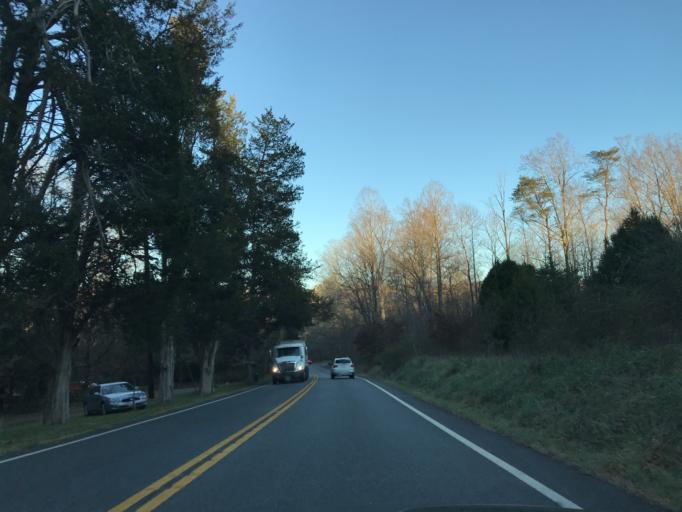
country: US
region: Maryland
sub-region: Howard County
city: Highland
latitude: 39.1602
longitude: -76.9776
